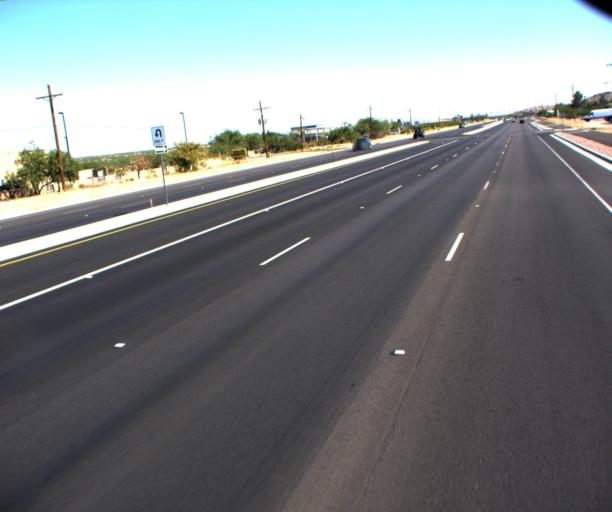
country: US
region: Arizona
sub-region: Pima County
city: Catalina
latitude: 32.5026
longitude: -110.9259
